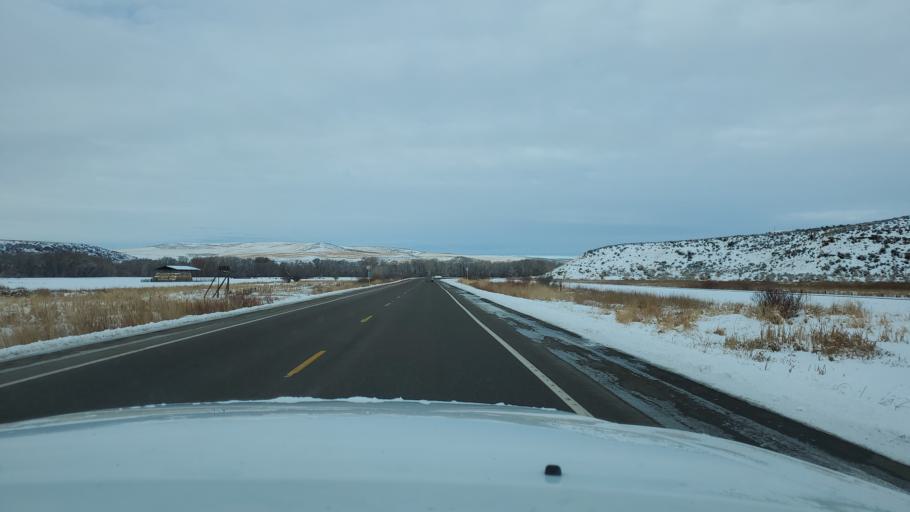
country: US
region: Colorado
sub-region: Routt County
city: Hayden
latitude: 40.4934
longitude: -107.3613
